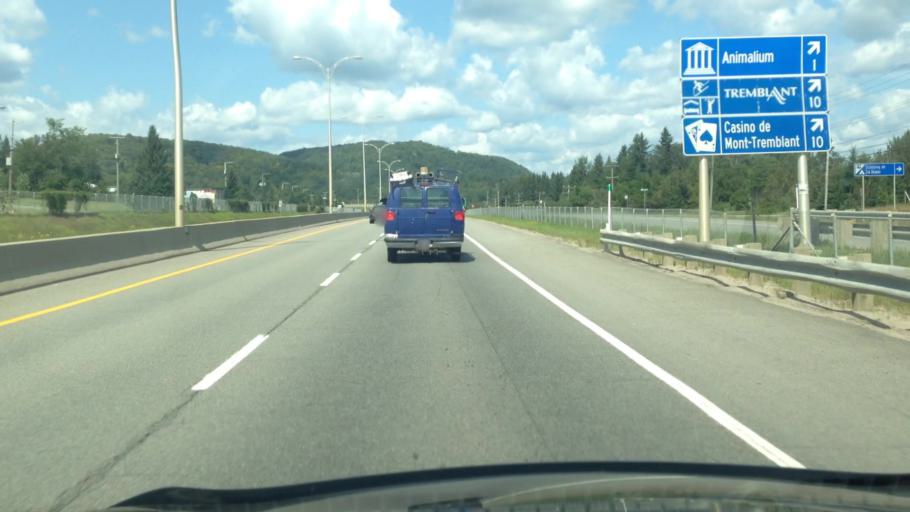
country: CA
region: Quebec
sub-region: Laurentides
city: Mont-Tremblant
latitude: 46.1251
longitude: -74.6085
